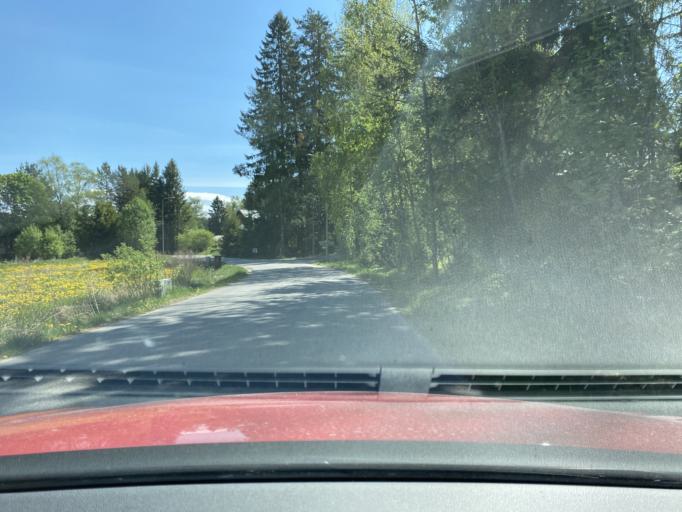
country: FI
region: Satakunta
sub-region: Rauma
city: Eura
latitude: 61.1103
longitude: 22.1362
